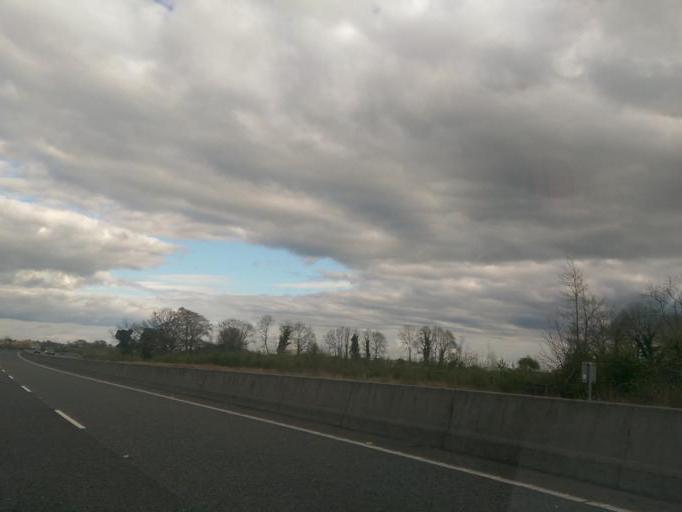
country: IE
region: Leinster
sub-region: Uibh Fhaili
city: Clara
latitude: 53.3934
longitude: -7.6252
